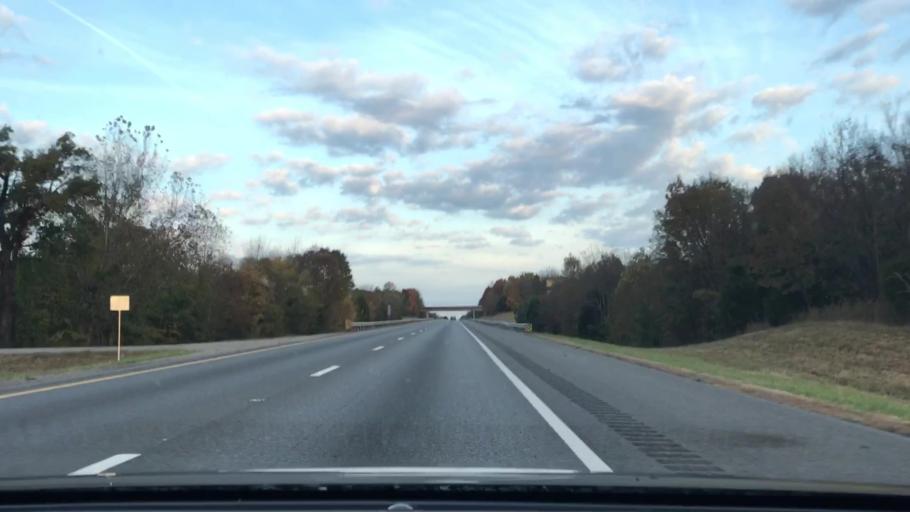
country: US
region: Tennessee
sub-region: Cheatham County
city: Pleasant View
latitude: 36.4744
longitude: -87.1372
